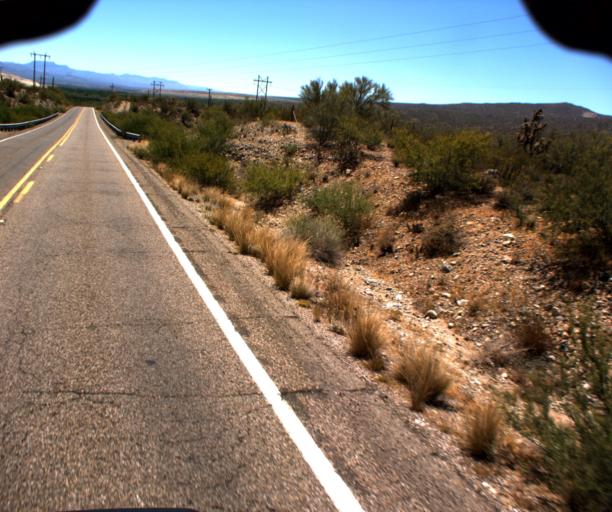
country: US
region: Arizona
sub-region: Pinal County
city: Kearny
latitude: 33.0193
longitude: -110.8486
